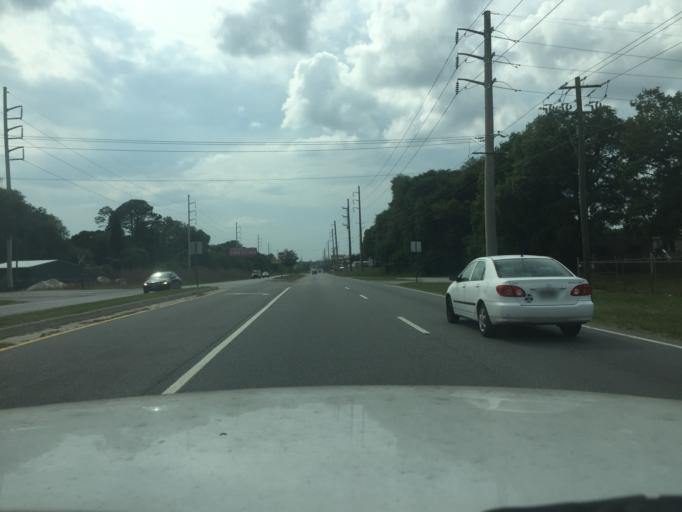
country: US
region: Georgia
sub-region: Chatham County
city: Thunderbolt
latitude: 32.0704
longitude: -81.0585
